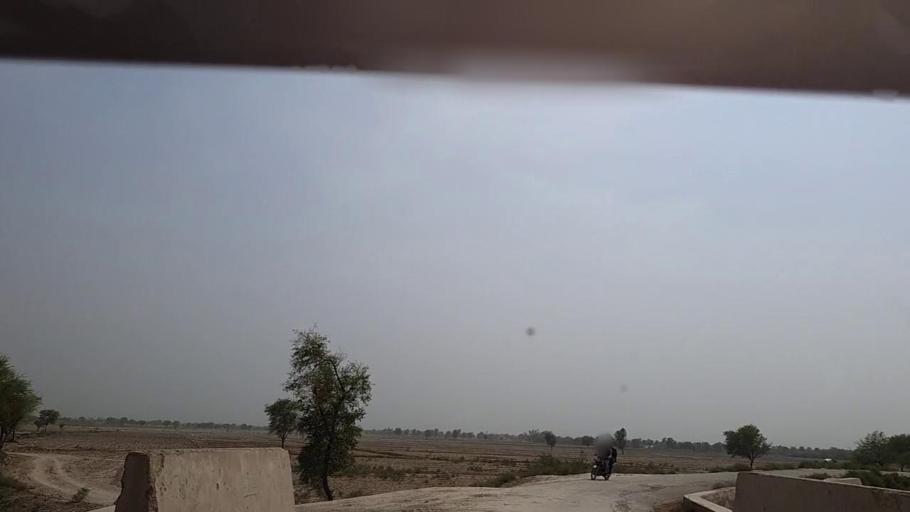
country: PK
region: Sindh
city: Khairpur Nathan Shah
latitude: 27.0330
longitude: 67.6816
